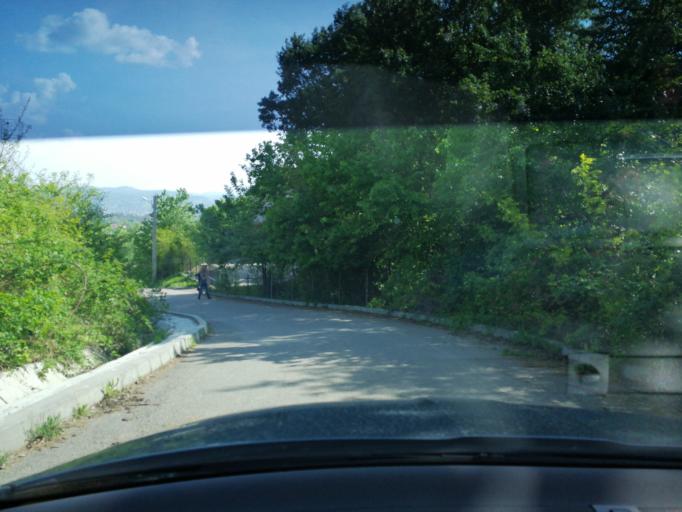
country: RO
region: Prahova
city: Cornu de Sus
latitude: 45.1690
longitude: 25.7061
